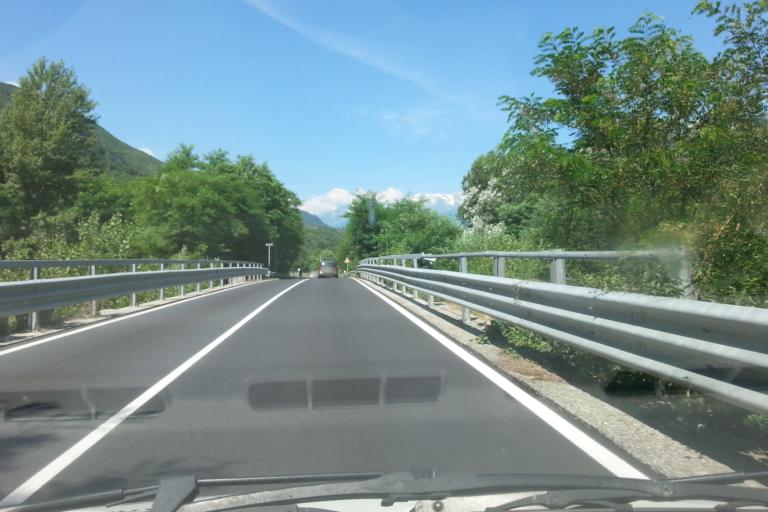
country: IT
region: Piedmont
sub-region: Provincia di Torino
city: Borgone Susa
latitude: 45.1193
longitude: 7.2224
